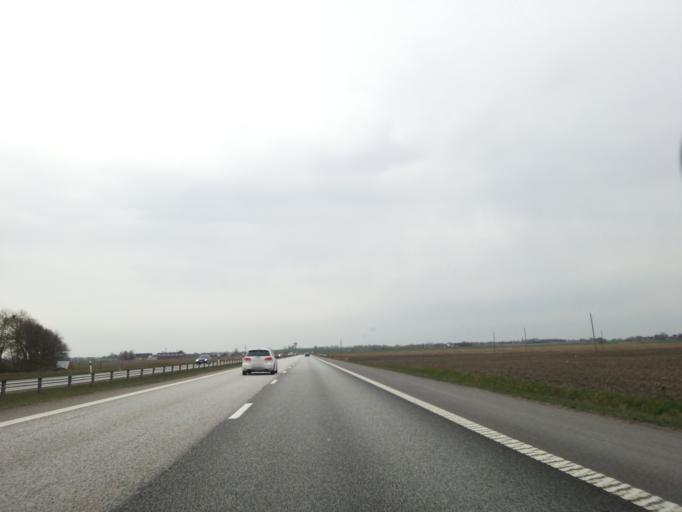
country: SE
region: Skane
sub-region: Angelholms Kommun
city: AEngelholm
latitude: 56.2831
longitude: 12.8989
